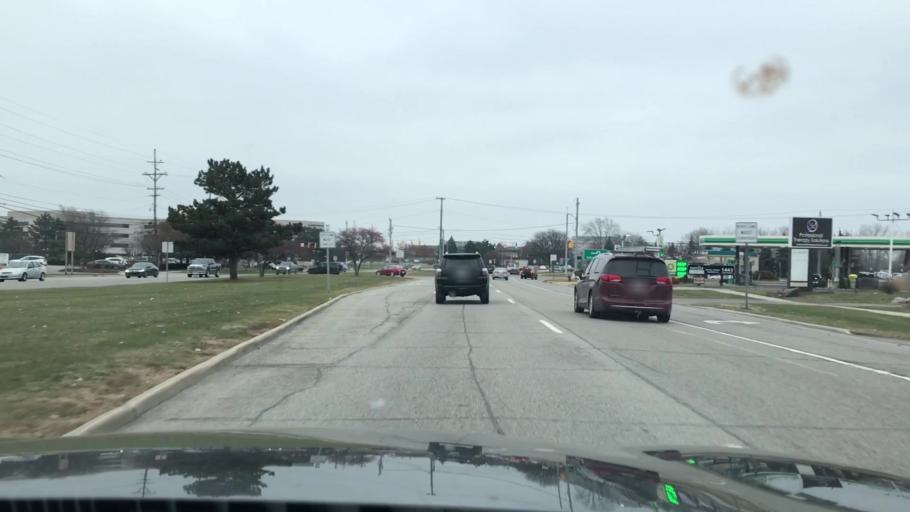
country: US
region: Michigan
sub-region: Oakland County
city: Clawson
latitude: 42.5501
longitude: -83.1228
